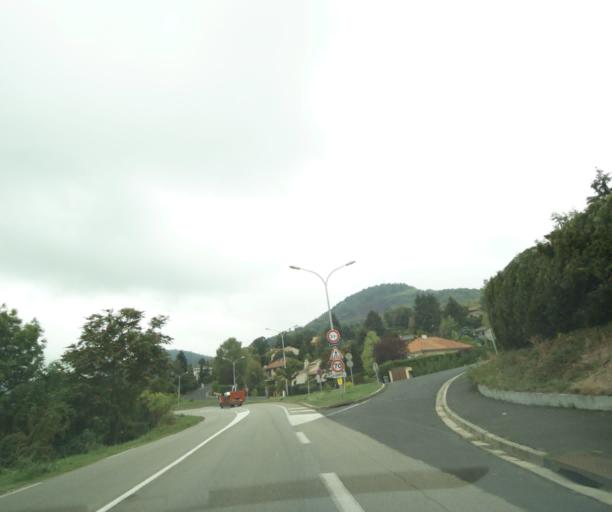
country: FR
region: Auvergne
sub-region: Departement du Puy-de-Dome
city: Royat
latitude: 45.7542
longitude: 3.0634
